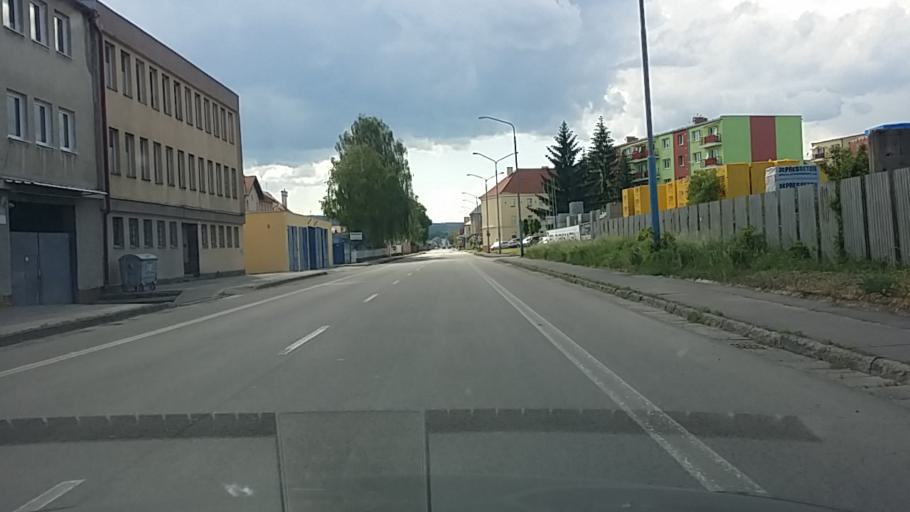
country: SK
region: Banskobystricky
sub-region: Okres Banska Bystrica
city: Zvolen
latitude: 48.5733
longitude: 19.1482
